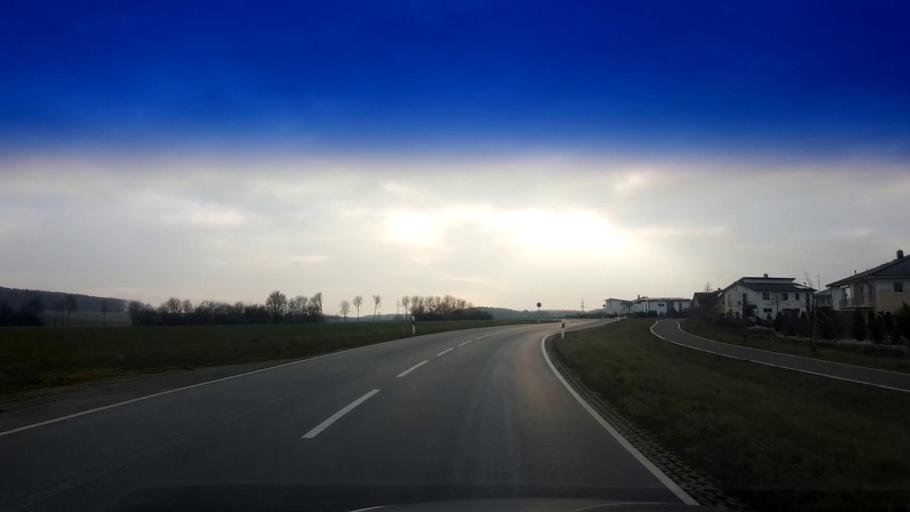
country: DE
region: Bavaria
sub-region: Upper Franconia
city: Hirschaid
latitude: 49.7994
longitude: 10.9714
